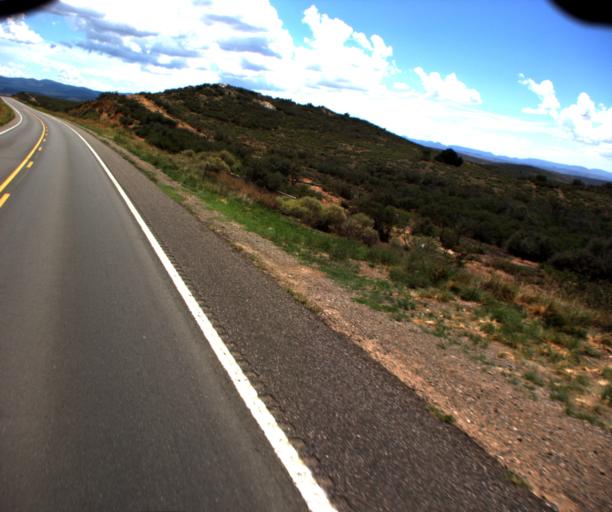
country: US
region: Arizona
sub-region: Yavapai County
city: Dewey-Humboldt
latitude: 34.5357
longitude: -112.1406
